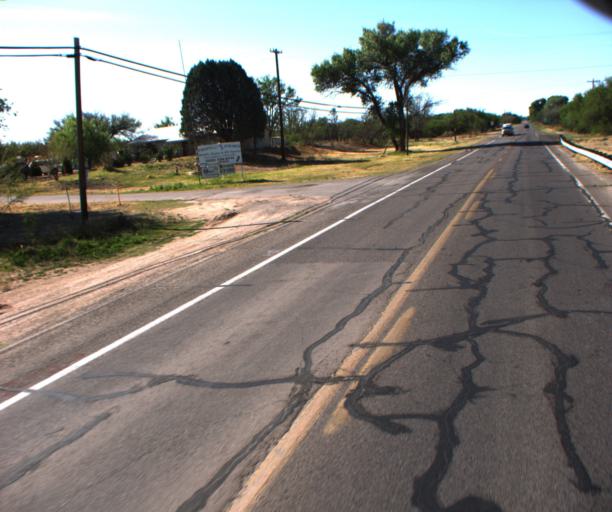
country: US
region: Arizona
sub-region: Cochise County
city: Saint David
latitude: 31.9000
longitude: -110.2135
